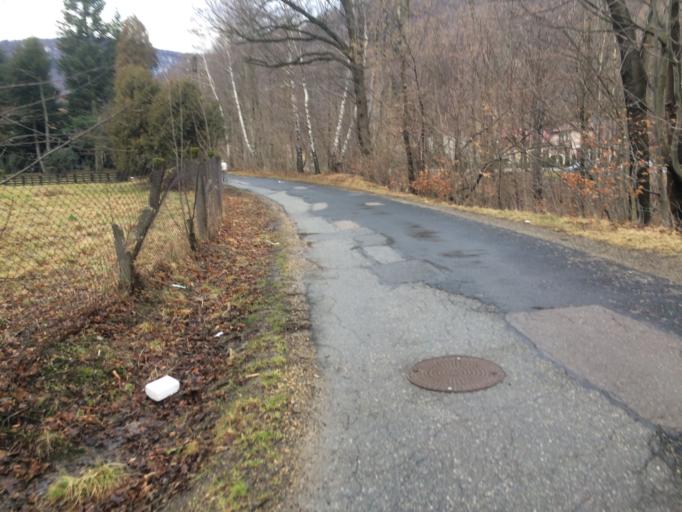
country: PL
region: Silesian Voivodeship
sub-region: Powiat bielski
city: Bystra
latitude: 49.7599
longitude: 19.0338
